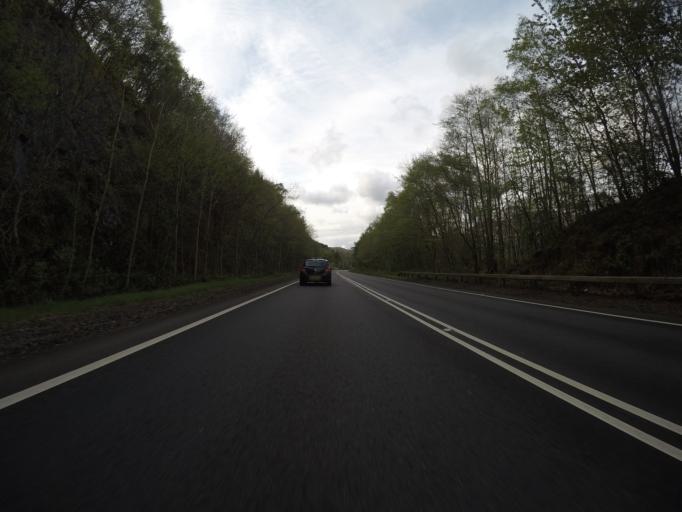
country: GB
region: Scotland
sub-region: Argyll and Bute
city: Helensburgh
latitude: 56.1424
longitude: -4.6628
